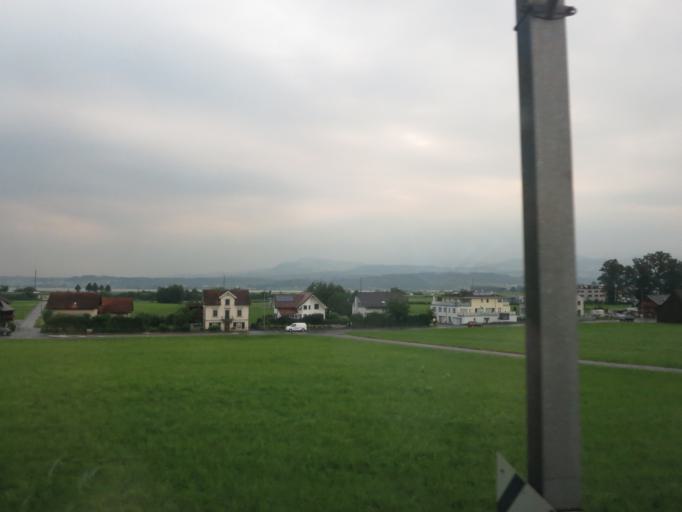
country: CH
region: Schwyz
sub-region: Bezirk March
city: Lachen
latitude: 47.1914
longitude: 8.8738
